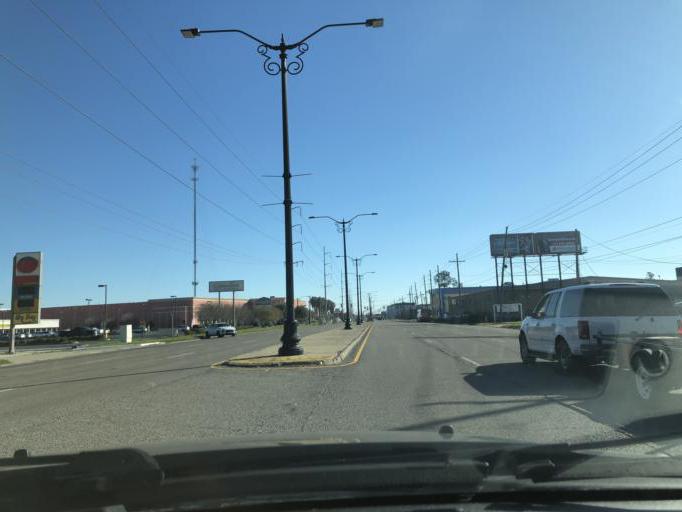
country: US
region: Louisiana
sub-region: Jefferson Parish
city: Jefferson
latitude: 29.9738
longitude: -90.1477
